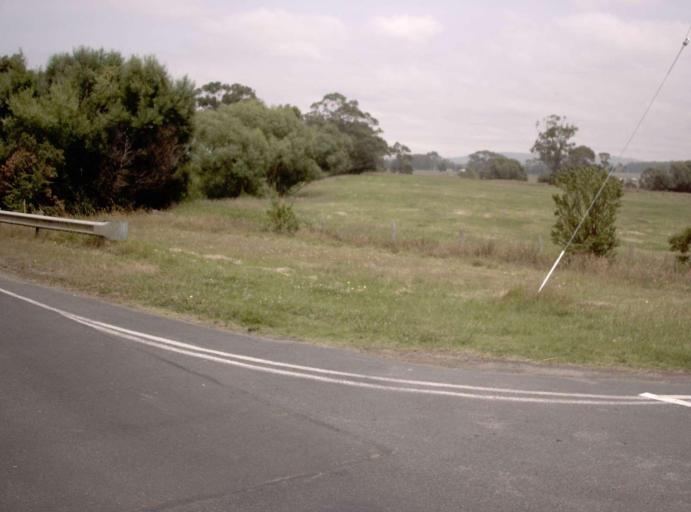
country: AU
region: Victoria
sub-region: Latrobe
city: Traralgon
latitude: -38.4659
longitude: 146.7185
